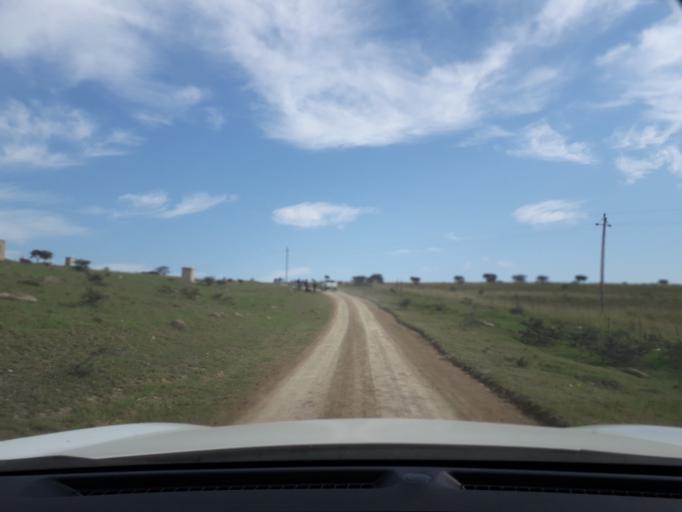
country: ZA
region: Eastern Cape
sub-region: Buffalo City Metropolitan Municipality
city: Bhisho
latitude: -32.9975
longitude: 27.3328
